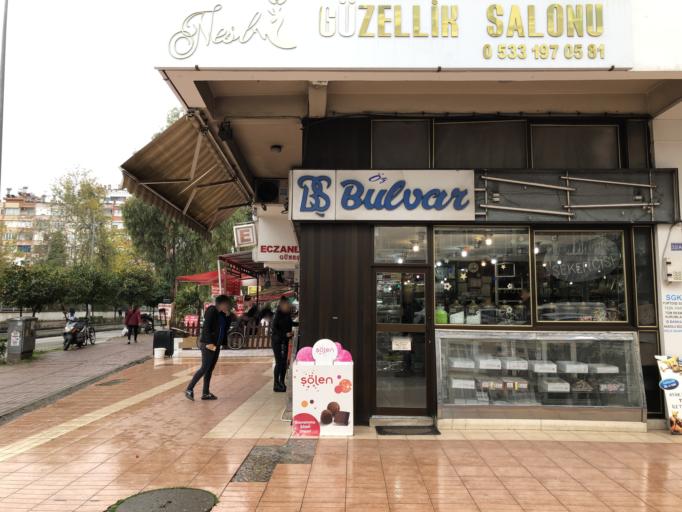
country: TR
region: Antalya
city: Antalya
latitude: 36.8945
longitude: 30.6924
